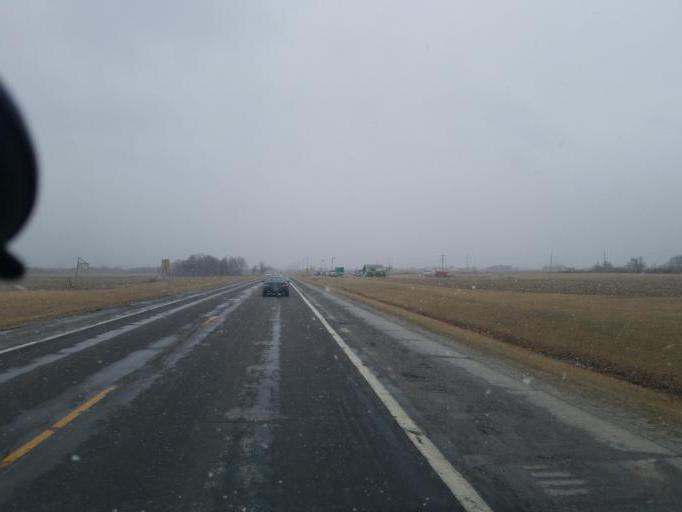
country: US
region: Missouri
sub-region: Schuyler County
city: Lancaster
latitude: 40.4023
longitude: -92.5590
